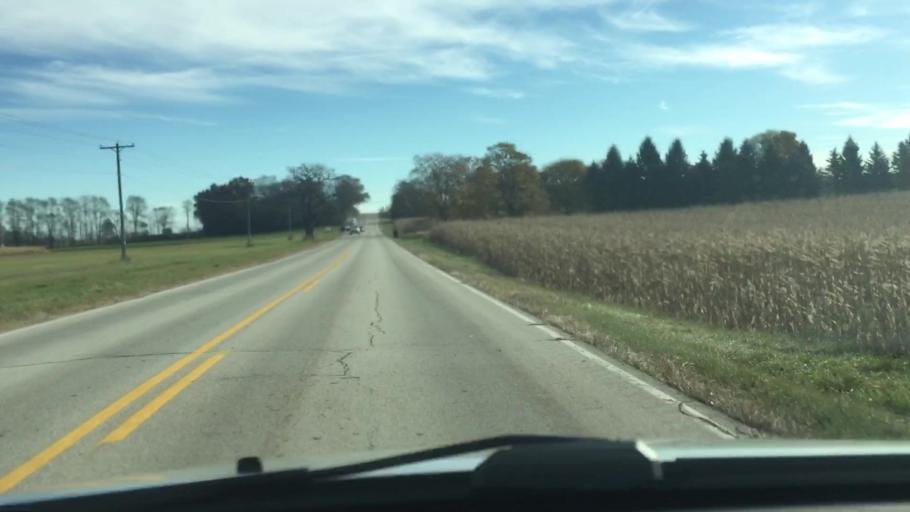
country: US
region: Wisconsin
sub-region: Waukesha County
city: North Prairie
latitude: 42.9449
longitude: -88.3946
